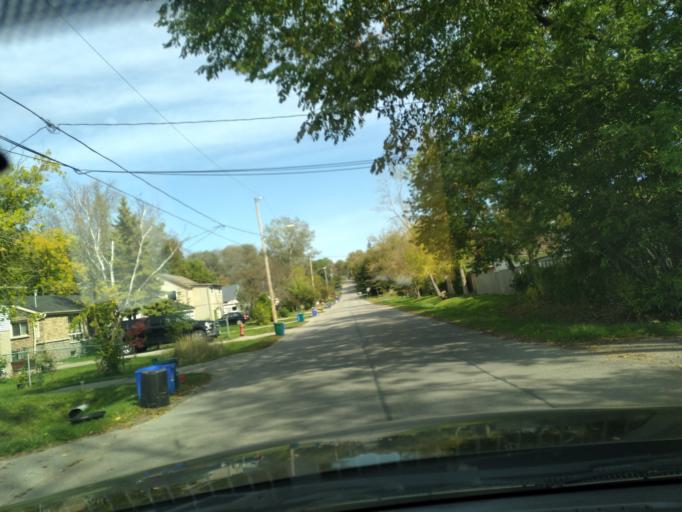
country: CA
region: Ontario
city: Keswick
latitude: 44.2066
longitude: -79.4741
